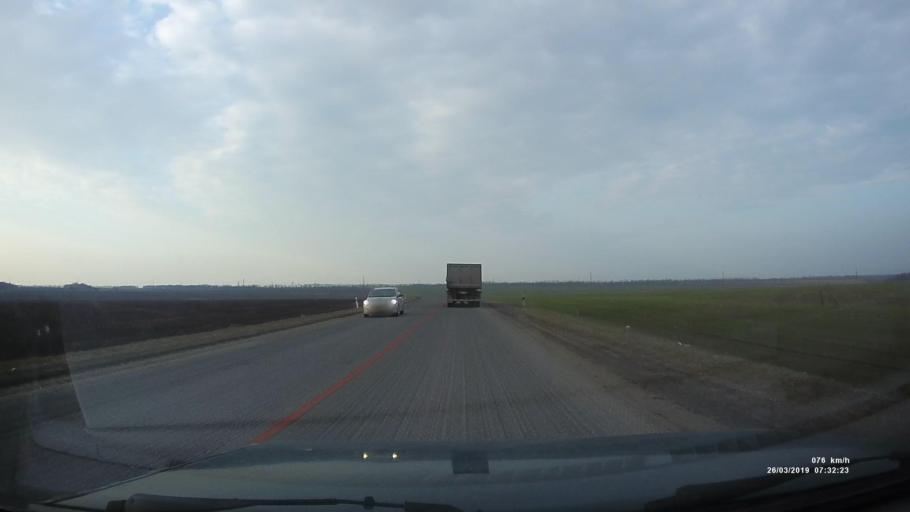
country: RU
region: Rostov
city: Novobessergenovka
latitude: 47.2261
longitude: 38.7782
